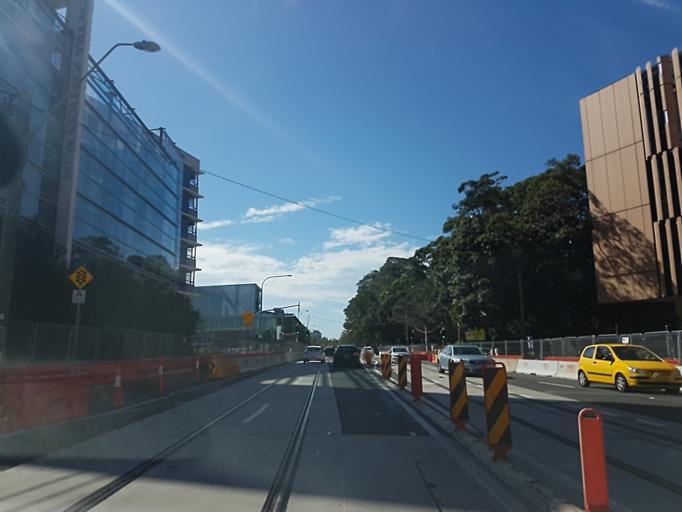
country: AU
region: New South Wales
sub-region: Randwick
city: Kensington
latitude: -33.9179
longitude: 151.2261
